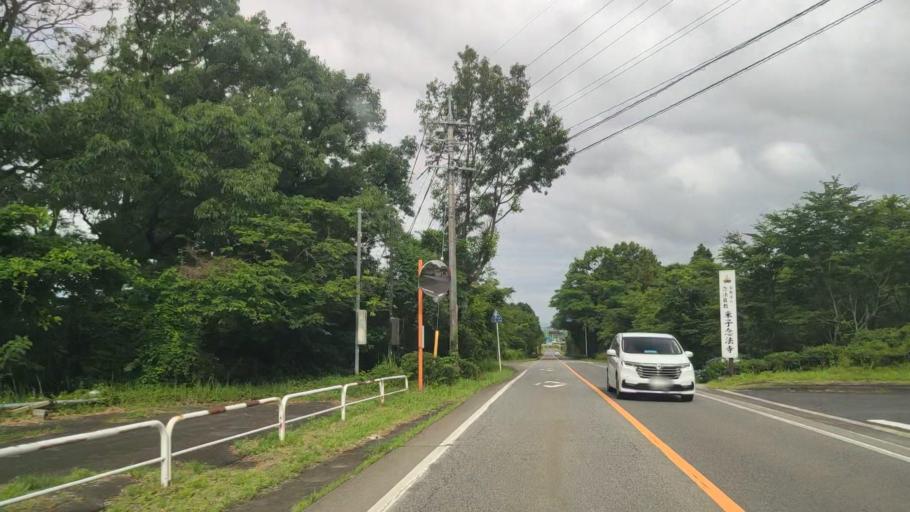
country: JP
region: Tottori
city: Yonago
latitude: 35.4231
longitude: 133.4206
